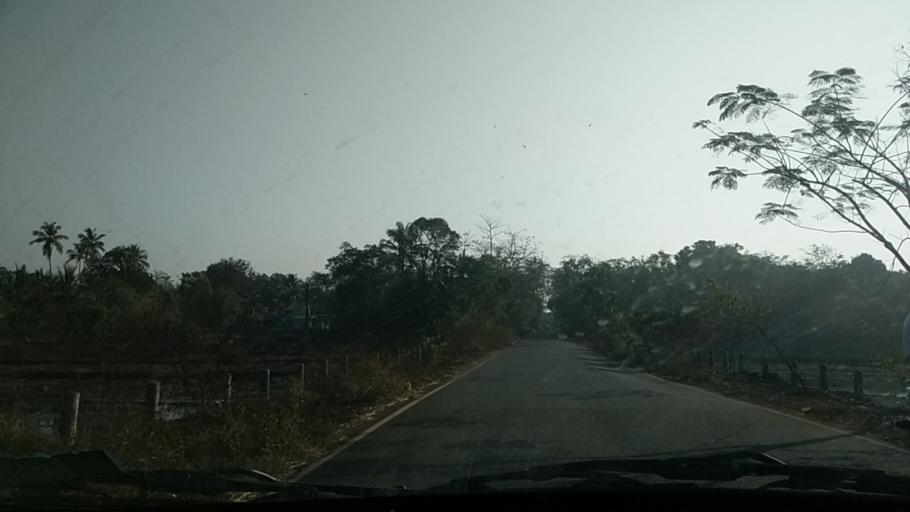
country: IN
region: Goa
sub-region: South Goa
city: Cuncolim
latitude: 15.1908
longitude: 74.0360
